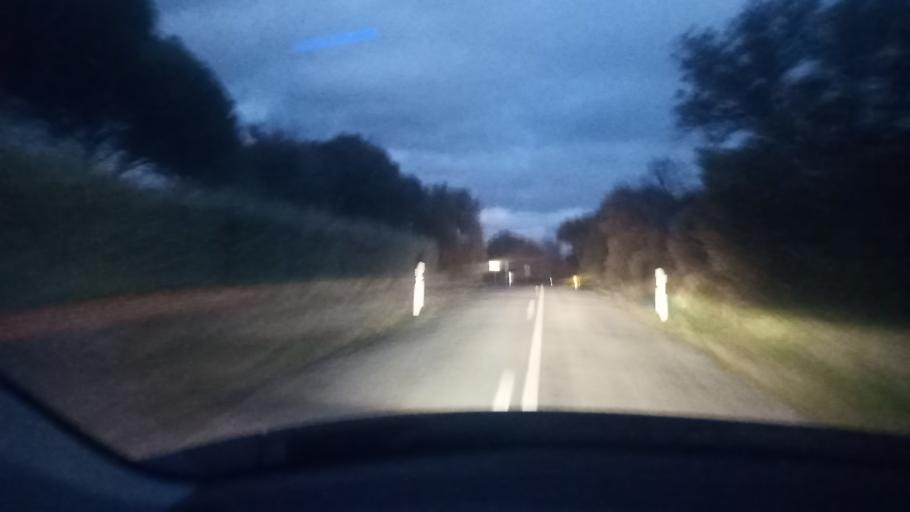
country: ES
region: Madrid
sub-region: Provincia de Madrid
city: Colmenar del Arroyo
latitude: 40.4294
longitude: -4.2123
